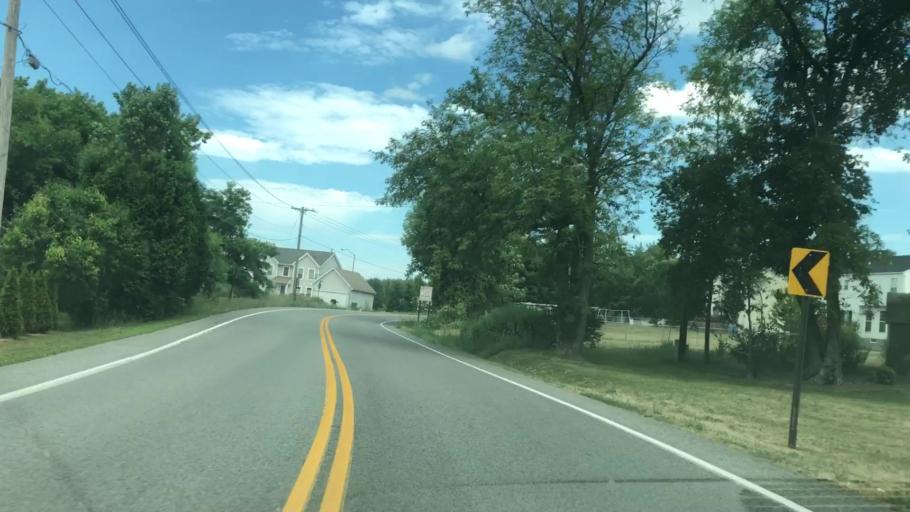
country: US
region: New York
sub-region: Wayne County
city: Macedon
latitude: 43.1232
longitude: -77.3528
